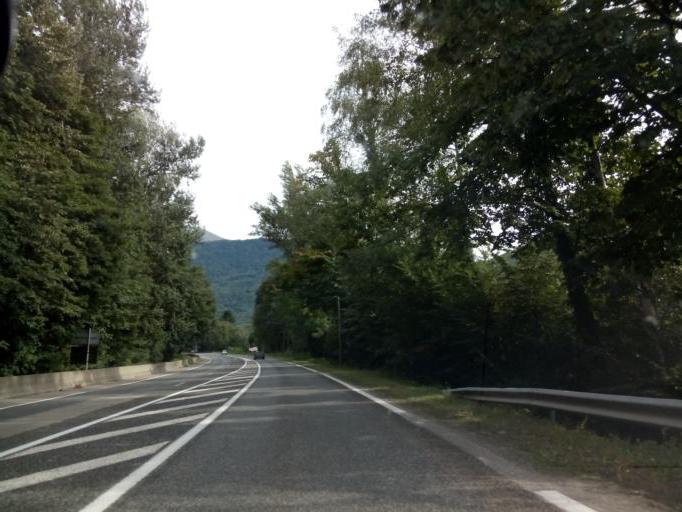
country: FR
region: Rhone-Alpes
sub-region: Departement de l'Isere
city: Notre-Dame-de-Mesage
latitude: 45.0629
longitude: 5.7632
